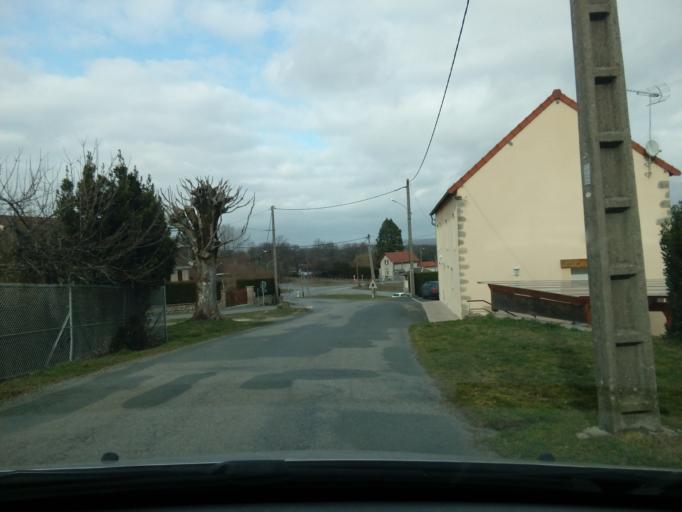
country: FR
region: Limousin
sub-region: Departement de la Creuse
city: Sainte-Feyre
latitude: 46.1403
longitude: 1.9247
